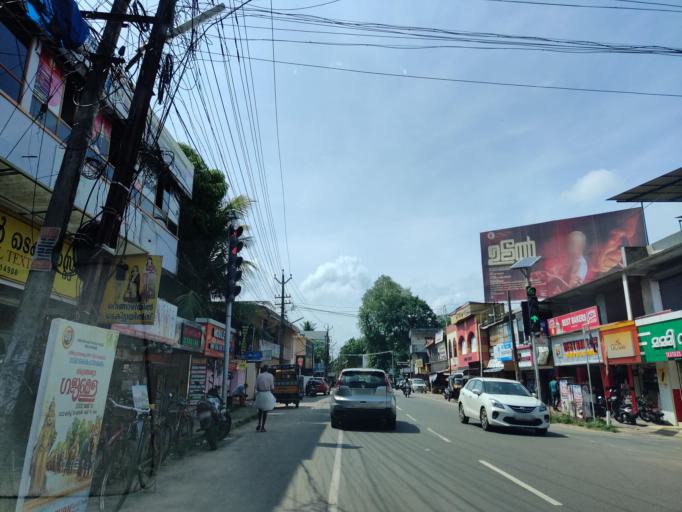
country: IN
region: Kerala
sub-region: Alappuzha
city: Mavelikara
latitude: 9.3114
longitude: 76.5341
